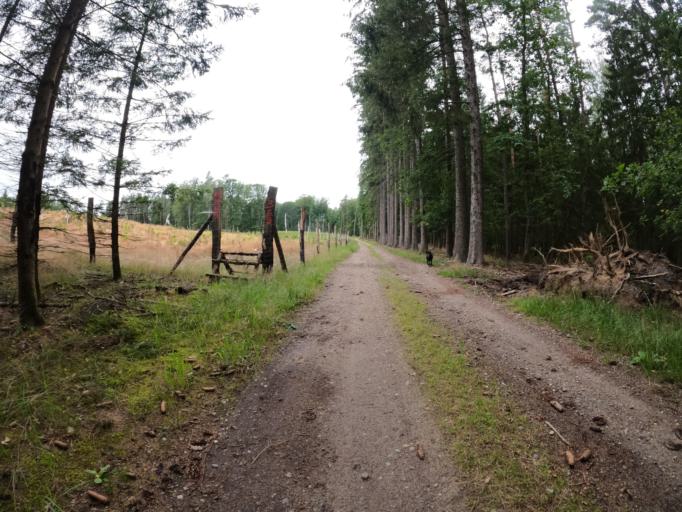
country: PL
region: West Pomeranian Voivodeship
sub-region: Powiat szczecinecki
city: Grzmiaca
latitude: 53.9763
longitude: 16.4221
